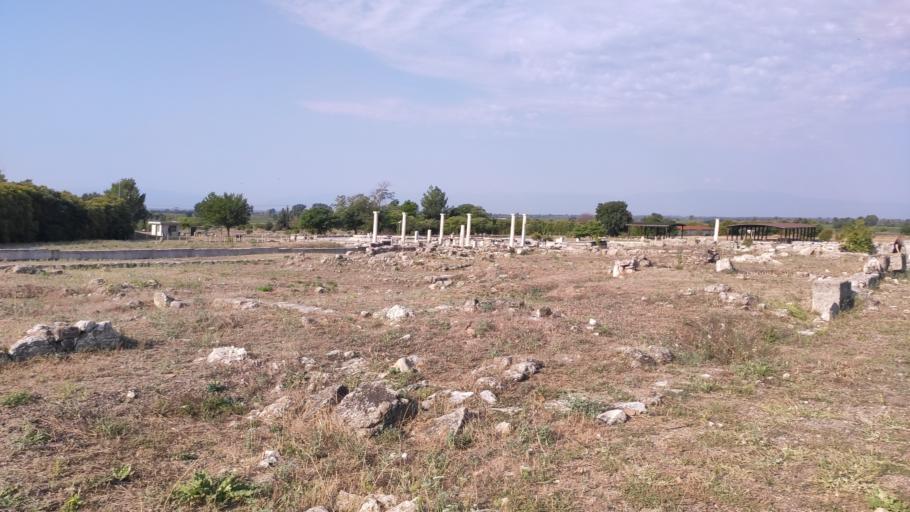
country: GR
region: Central Macedonia
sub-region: Nomos Pellis
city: Pella
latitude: 40.7549
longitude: 22.5197
